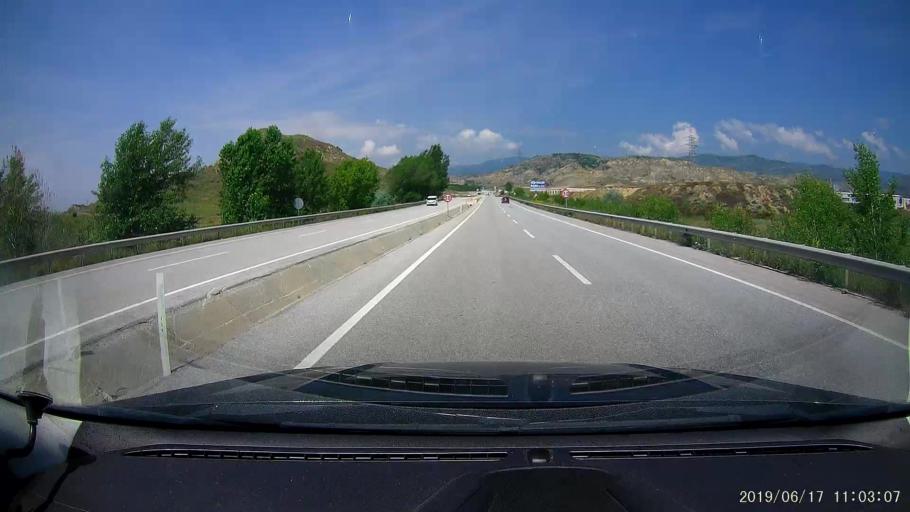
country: TR
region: Kastamonu
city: Tosya
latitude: 41.0160
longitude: 34.1217
